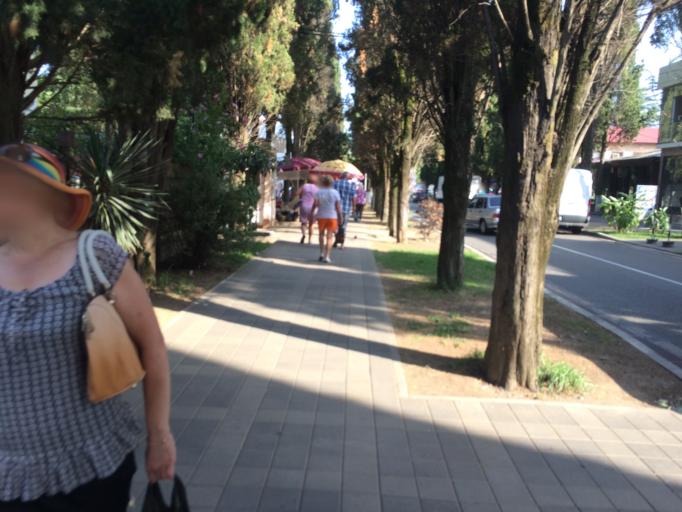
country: RU
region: Krasnodarskiy
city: Adler
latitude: 43.3912
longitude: 39.9840
